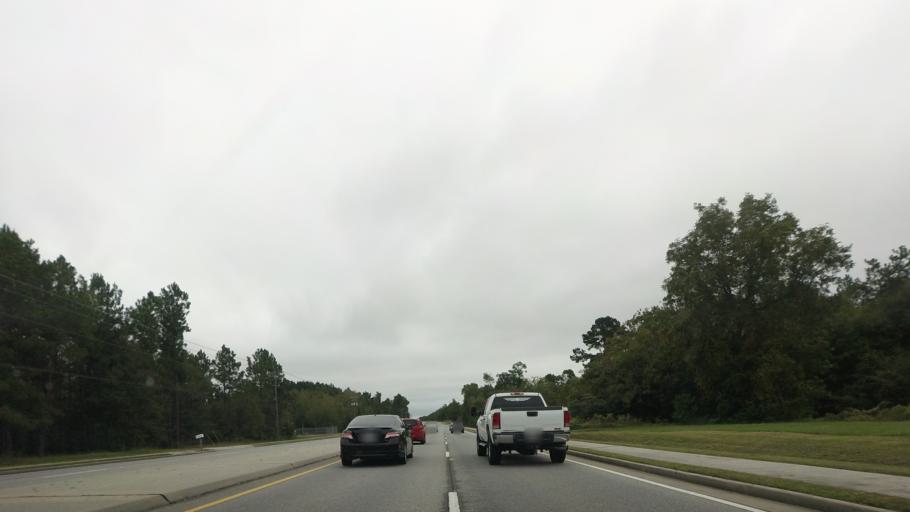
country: US
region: Georgia
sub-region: Lowndes County
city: Valdosta
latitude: 30.9487
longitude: -83.2310
